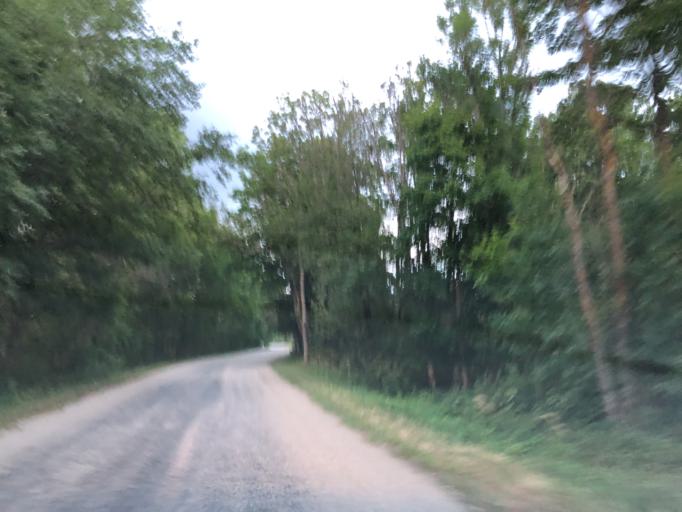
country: EE
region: Laeaene
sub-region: Ridala Parish
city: Uuemoisa
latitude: 58.8789
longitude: 23.6401
